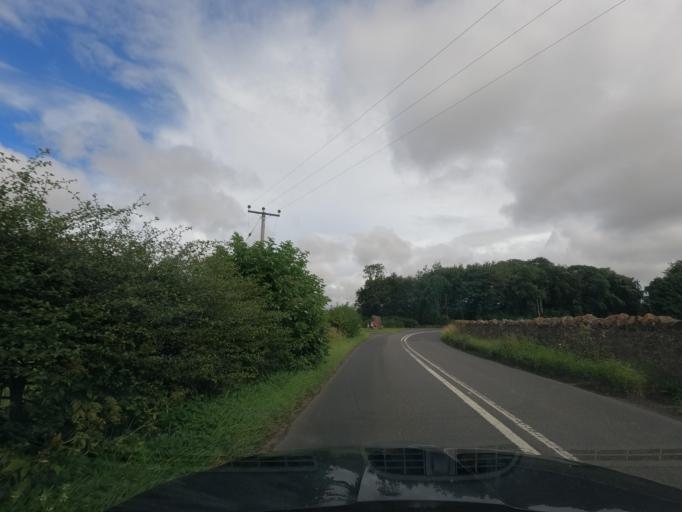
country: GB
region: England
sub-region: Northumberland
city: Lowick
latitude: 55.6517
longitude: -1.9977
